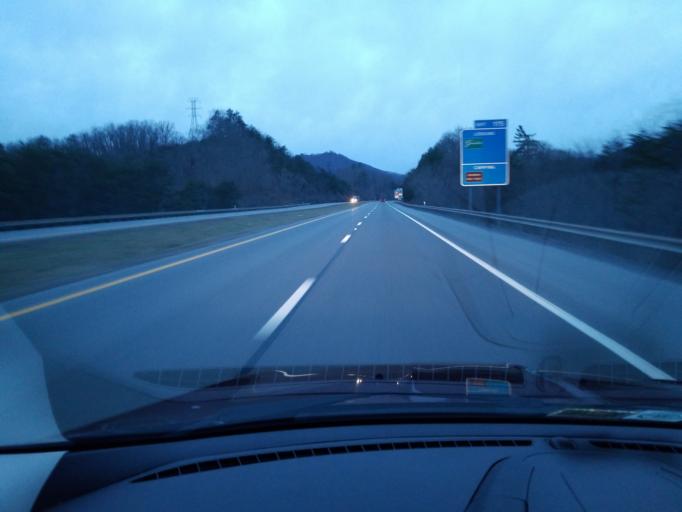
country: US
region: West Virginia
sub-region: Greenbrier County
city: White Sulphur Springs
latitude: 37.7703
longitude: -80.3297
